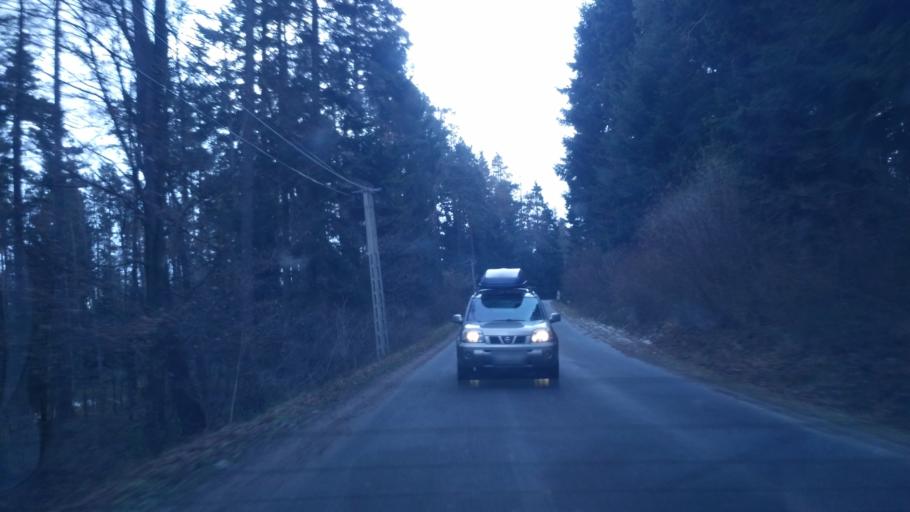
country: PL
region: Subcarpathian Voivodeship
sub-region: Powiat rzeszowski
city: Blazowa
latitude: 49.8574
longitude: 22.0974
